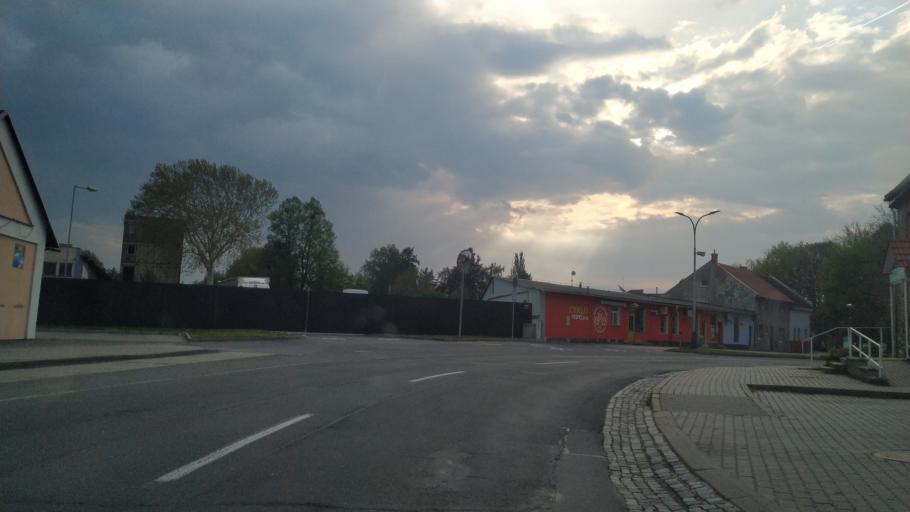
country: CZ
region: Olomoucky
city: Lutin
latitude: 49.5584
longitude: 17.1412
